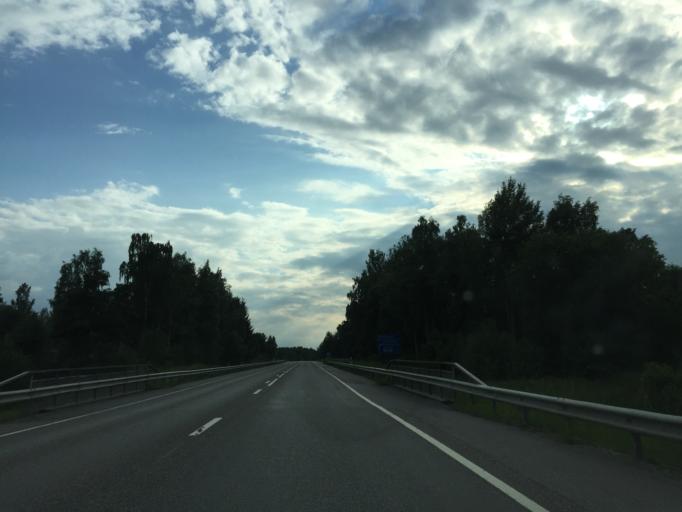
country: SE
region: OErebro
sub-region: Lindesbergs Kommun
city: Fellingsbro
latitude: 59.3531
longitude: 15.6697
